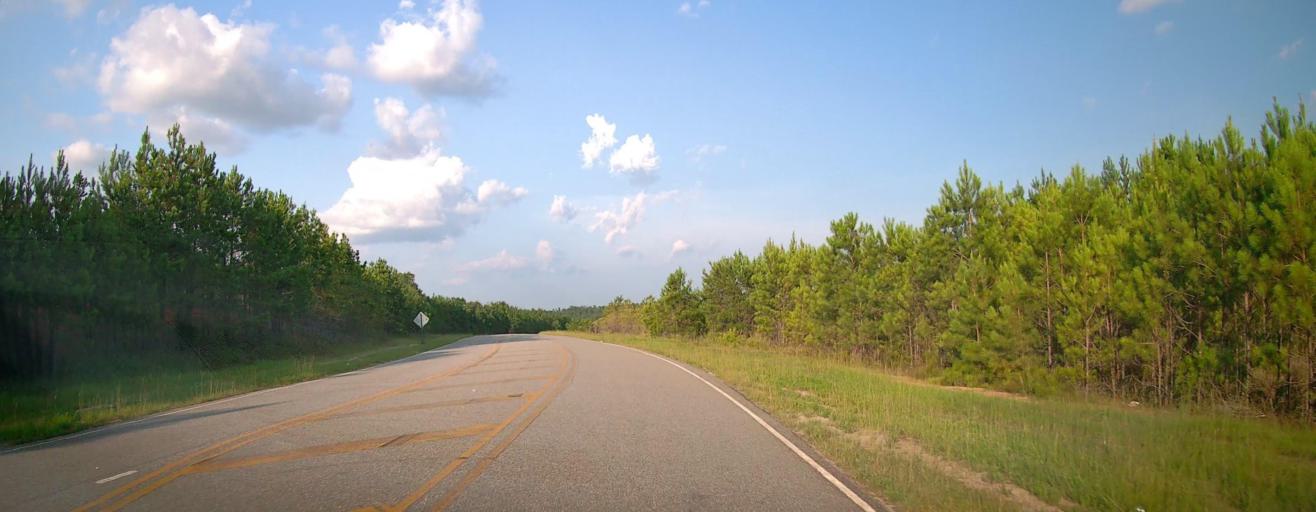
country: US
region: Georgia
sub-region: Peach County
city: Byron
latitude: 32.6794
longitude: -83.7631
